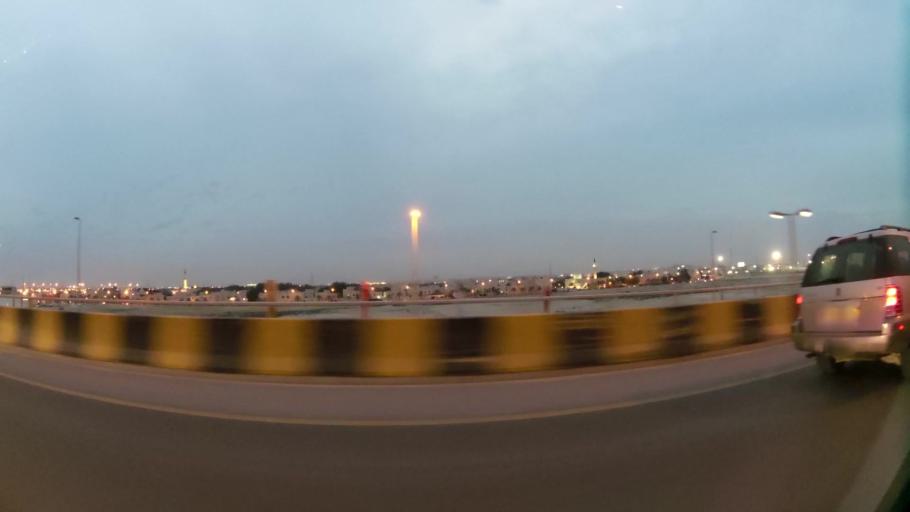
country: BH
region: Northern
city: Madinat `Isa
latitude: 26.1735
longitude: 50.5418
